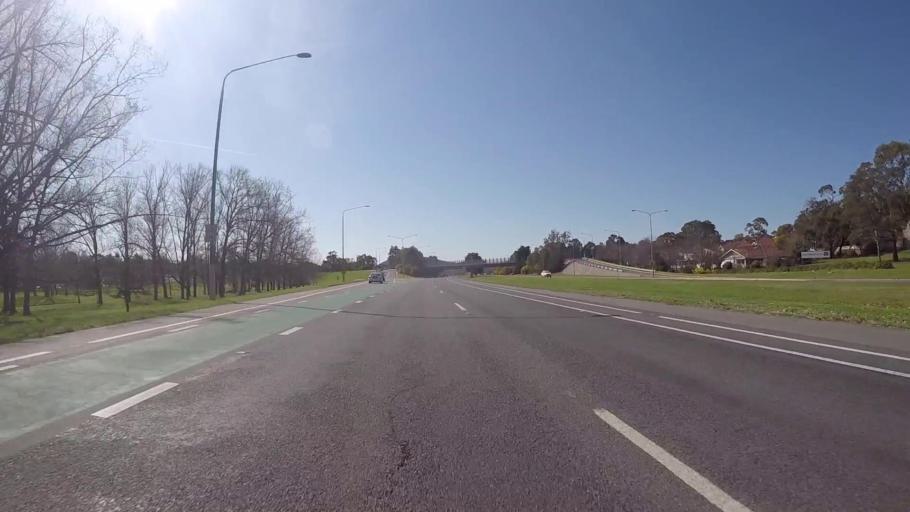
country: AU
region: Australian Capital Territory
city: Forrest
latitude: -35.3287
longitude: 149.0863
